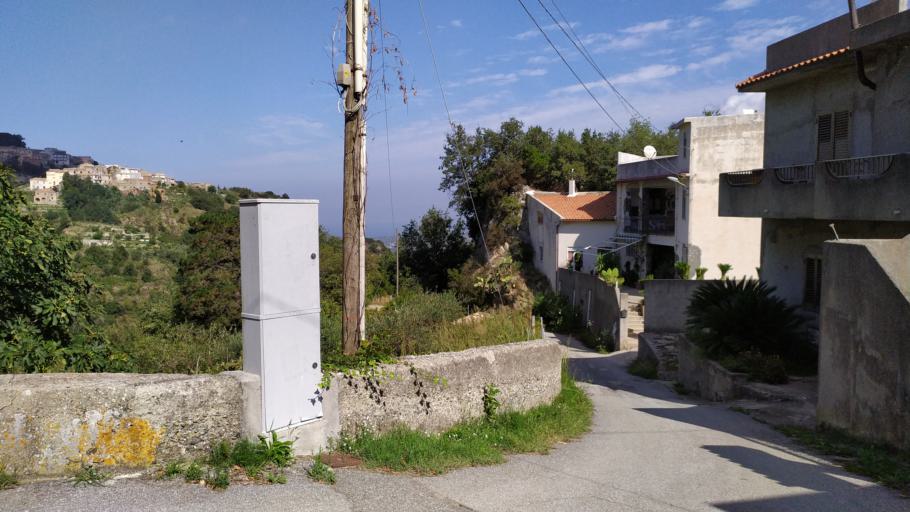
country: IT
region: Sicily
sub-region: Messina
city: Rometta
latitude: 38.1627
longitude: 15.4182
